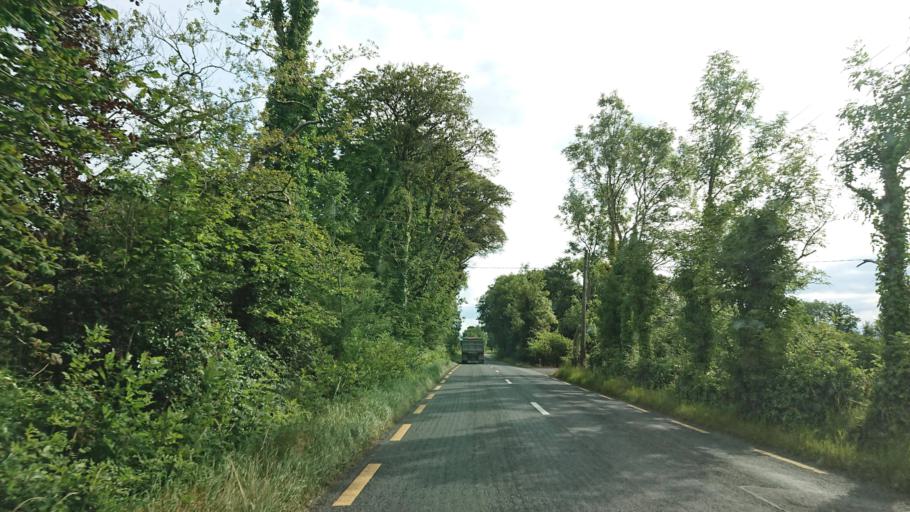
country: IE
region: Connaught
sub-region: County Leitrim
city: Carrick-on-Shannon
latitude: 53.9667
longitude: -8.0704
